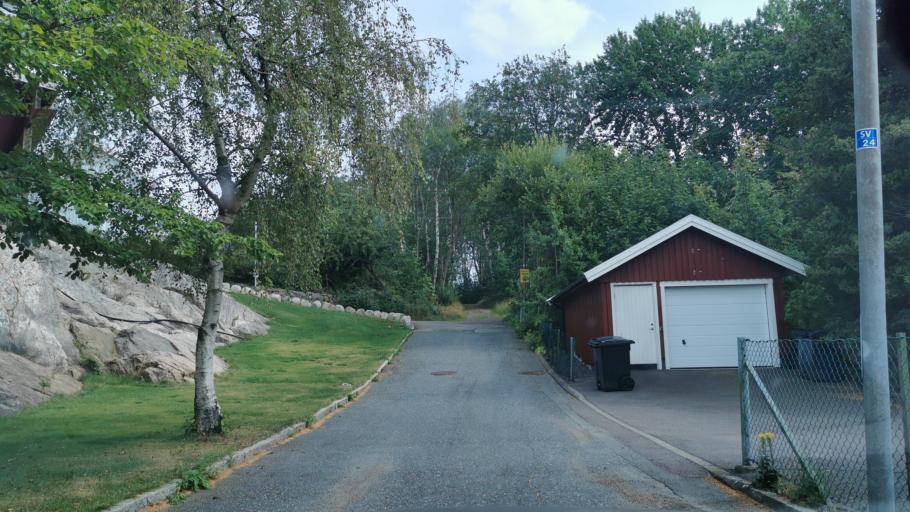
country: SE
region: Vaestra Goetaland
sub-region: Molndal
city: Moelndal
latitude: 57.6747
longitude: 11.9845
